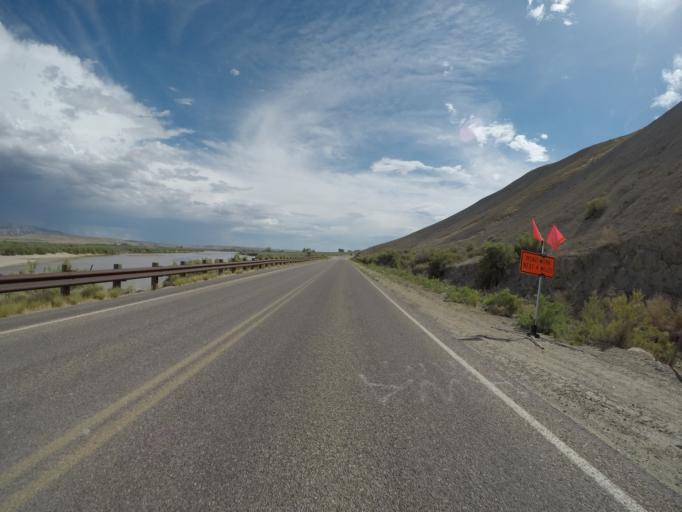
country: US
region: Utah
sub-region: Uintah County
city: Naples
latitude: 40.4343
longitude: -109.3309
